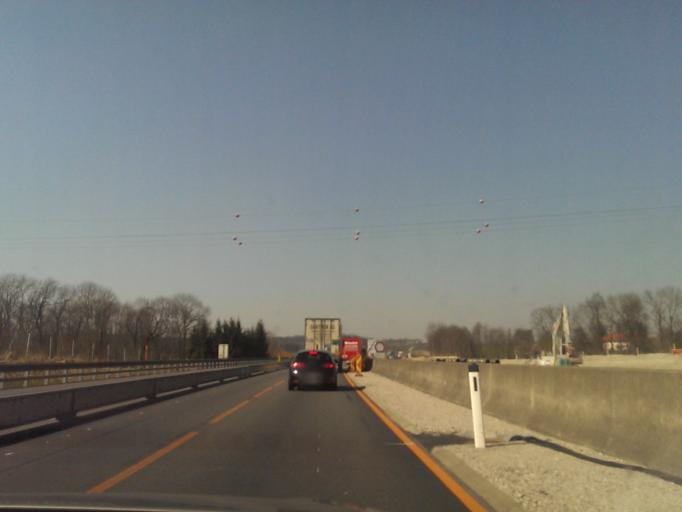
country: AT
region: Upper Austria
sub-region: Politischer Bezirk Vocklabruck
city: Wolfsegg am Hausruck
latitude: 48.1923
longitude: 13.6505
